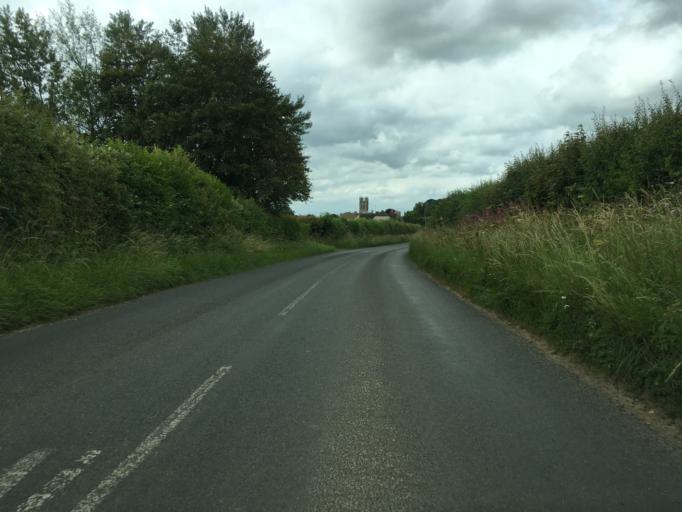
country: GB
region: England
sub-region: Oxfordshire
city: Chipping Norton
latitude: 51.9186
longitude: -1.5860
